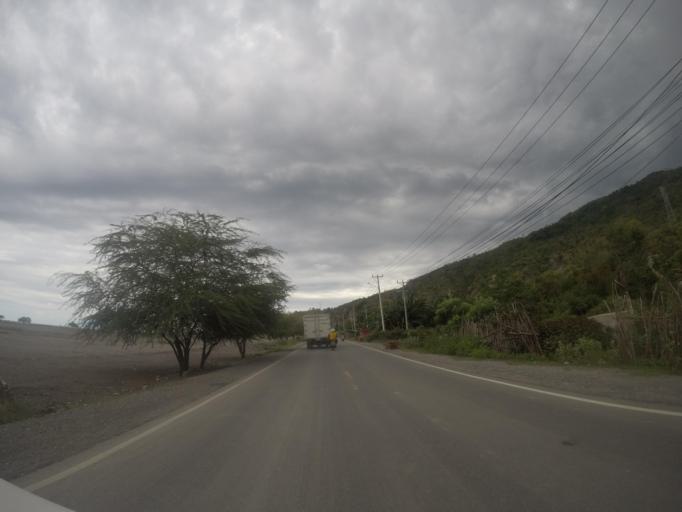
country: TL
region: Liquica
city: Liquica
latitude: -8.5793
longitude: 125.3630
